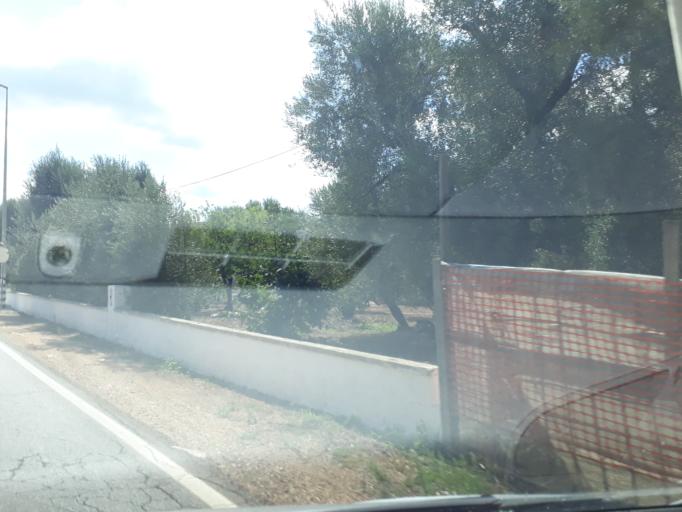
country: IT
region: Apulia
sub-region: Provincia di Brindisi
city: Fasano
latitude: 40.8188
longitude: 17.3773
